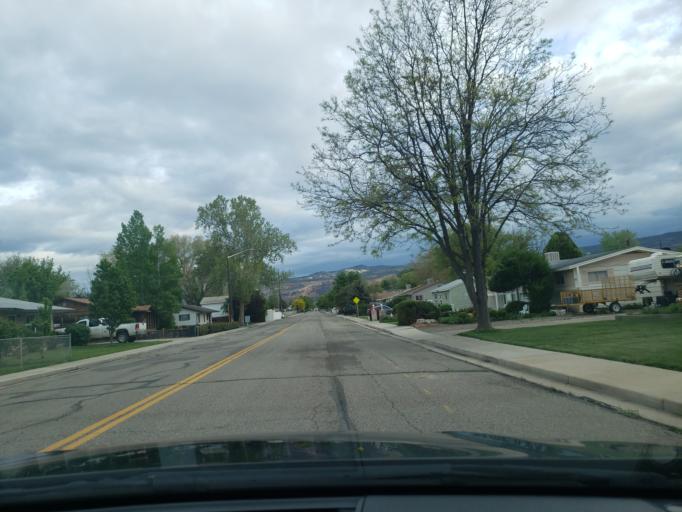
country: US
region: Colorado
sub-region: Mesa County
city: Fruita
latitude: 39.1658
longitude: -108.7314
